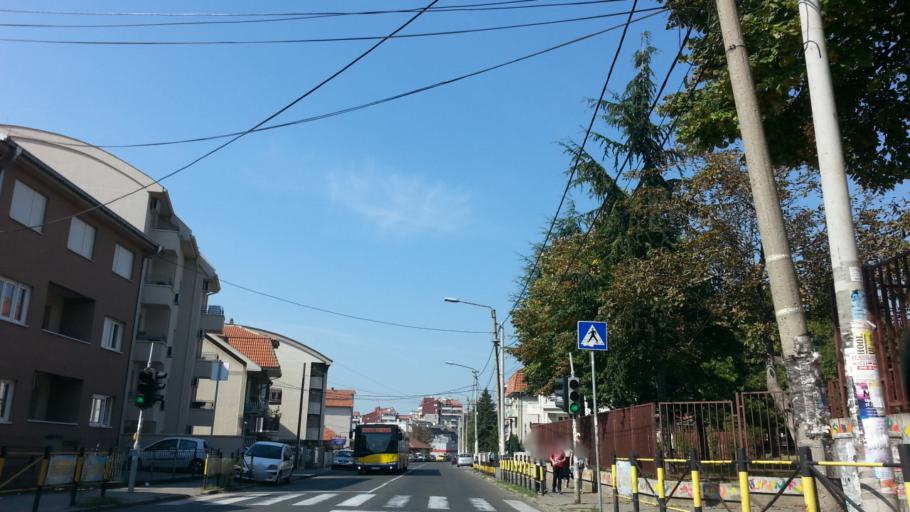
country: RS
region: Central Serbia
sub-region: Belgrade
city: Cukarica
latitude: 44.7575
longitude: 20.4187
